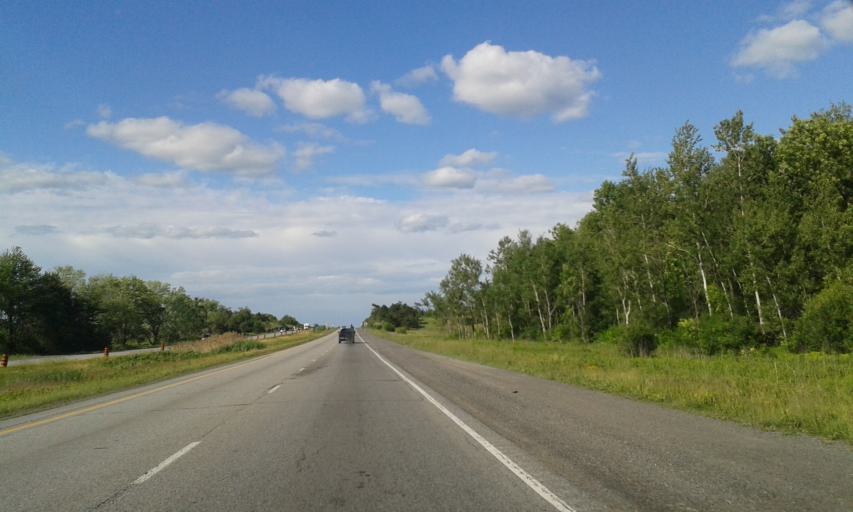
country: CA
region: Ontario
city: Prescott
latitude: 44.6975
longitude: -75.5726
